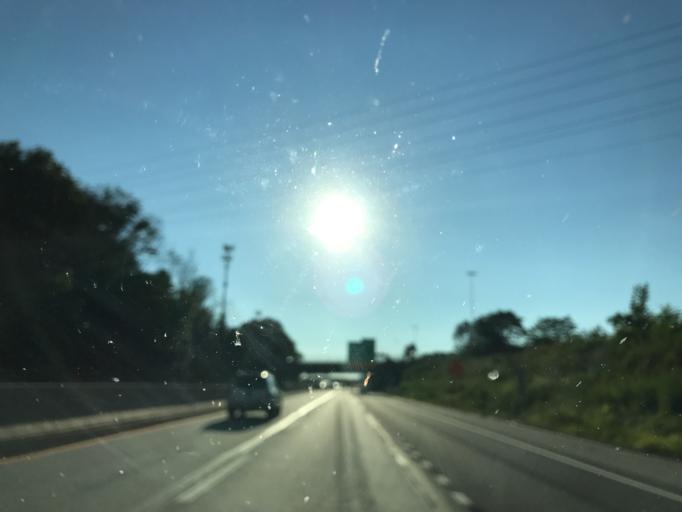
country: US
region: Pennsylvania
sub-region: Bucks County
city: Trevose
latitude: 40.1307
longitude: -74.9650
